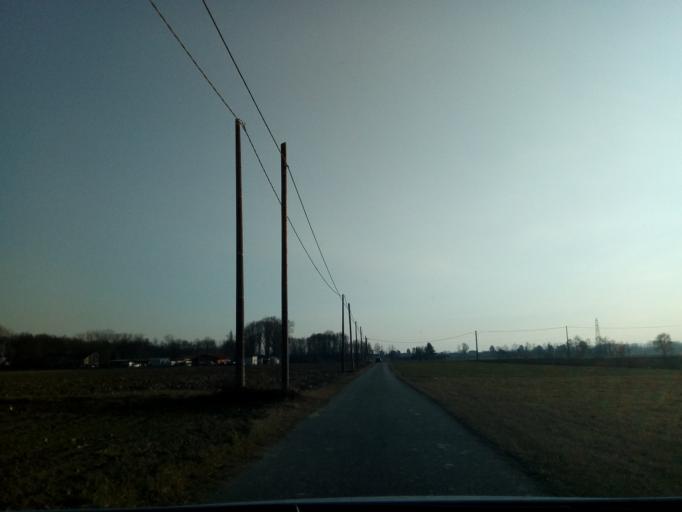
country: IT
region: Piedmont
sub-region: Provincia di Torino
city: Cascinette d'Ivrea
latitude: 45.4639
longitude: 7.9139
